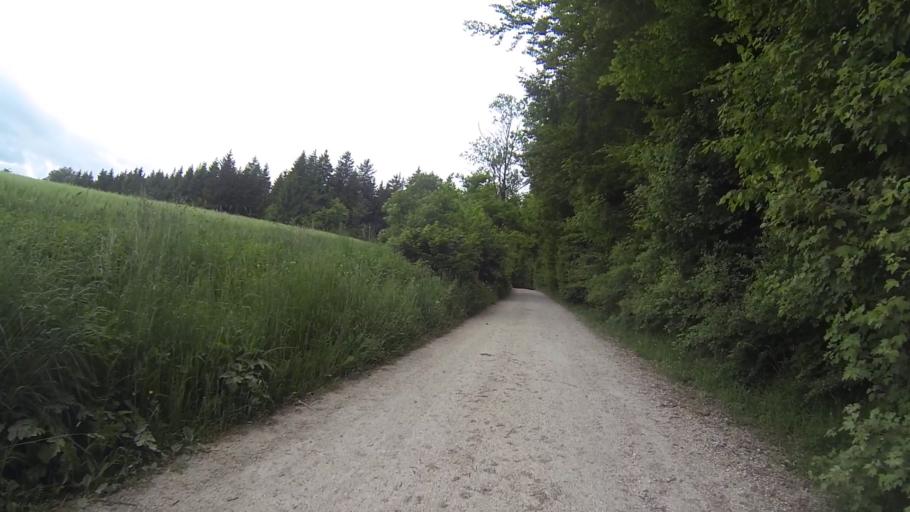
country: DE
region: Baden-Wuerttemberg
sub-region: Regierungsbezirk Stuttgart
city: Essingen
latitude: 48.7794
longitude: 10.0364
